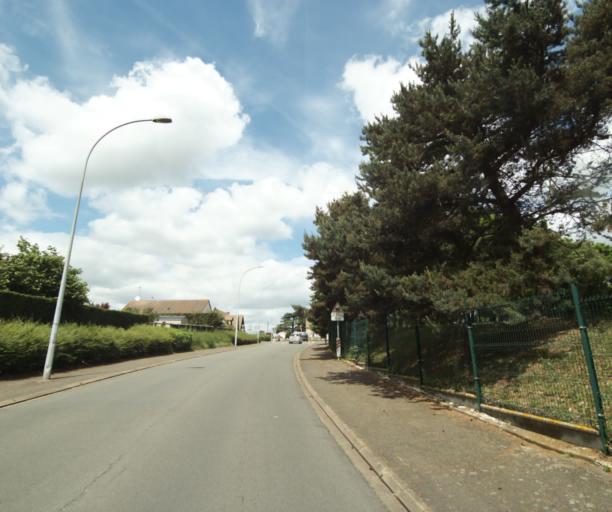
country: FR
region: Centre
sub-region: Departement d'Eure-et-Loir
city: Mainvilliers
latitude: 48.4455
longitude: 1.4609
